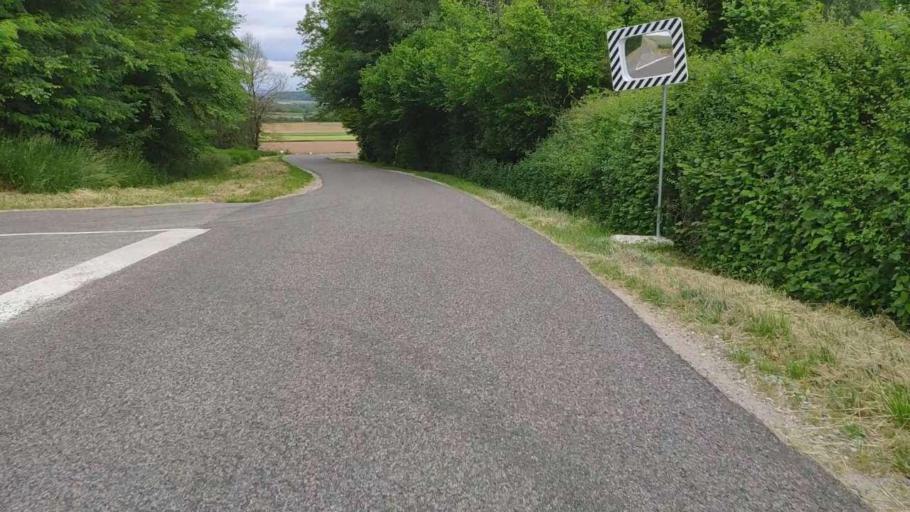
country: FR
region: Franche-Comte
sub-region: Departement du Jura
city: Bletterans
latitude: 46.7782
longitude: 5.5054
